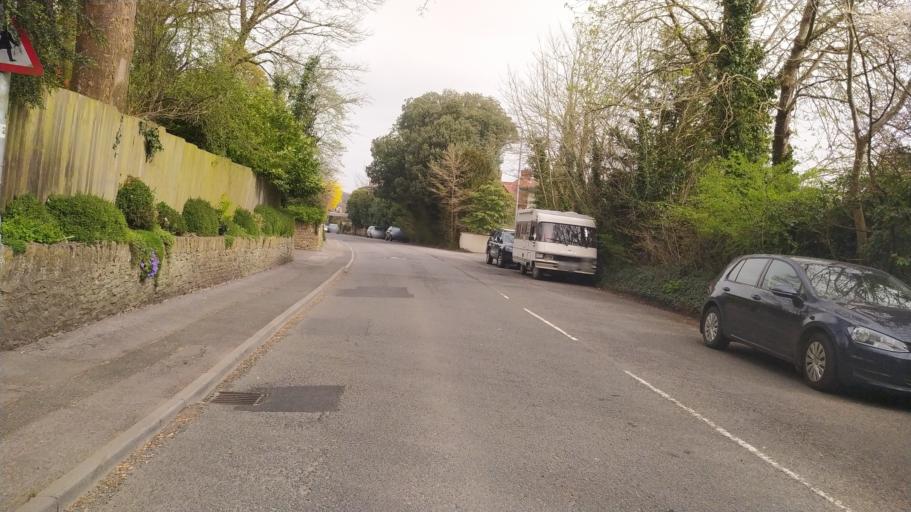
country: GB
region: England
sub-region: Somerset
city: Frome
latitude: 51.2347
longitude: -2.3162
